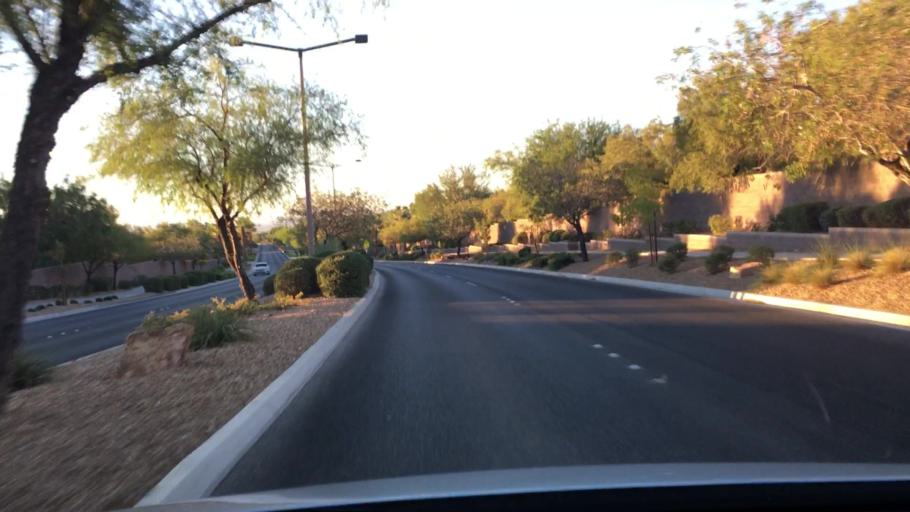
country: US
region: Nevada
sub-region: Clark County
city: Summerlin South
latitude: 36.1305
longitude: -115.3426
